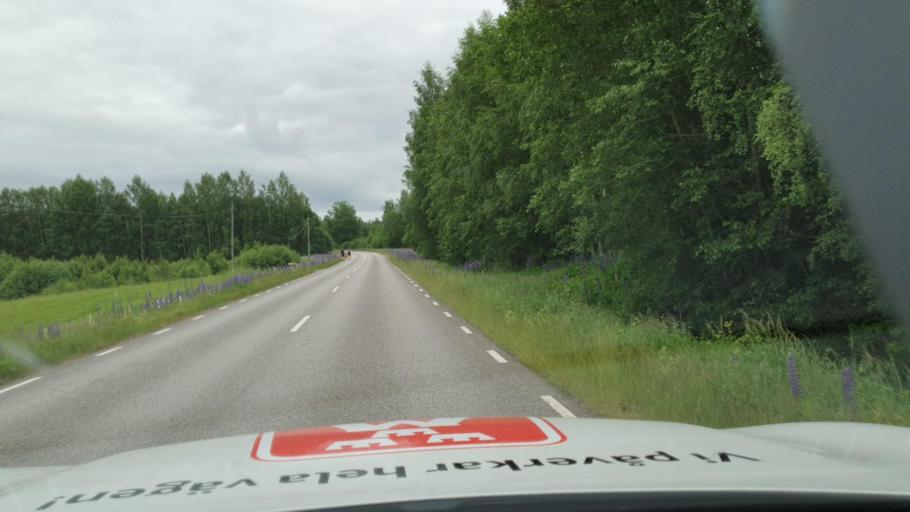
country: SE
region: Vaermland
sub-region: Sunne Kommun
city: Sunne
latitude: 59.8093
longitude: 13.0313
